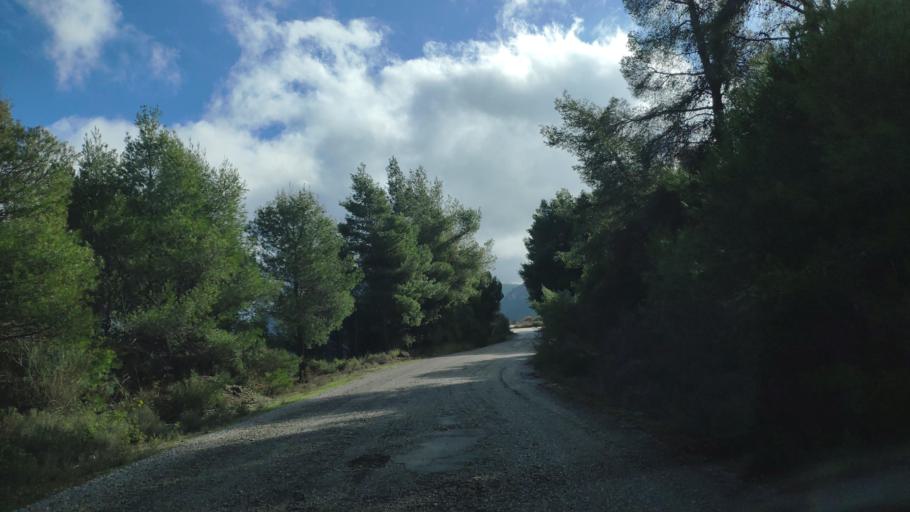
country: GR
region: West Greece
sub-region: Nomos Achaias
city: Aiyira
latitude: 38.1013
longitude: 22.4460
